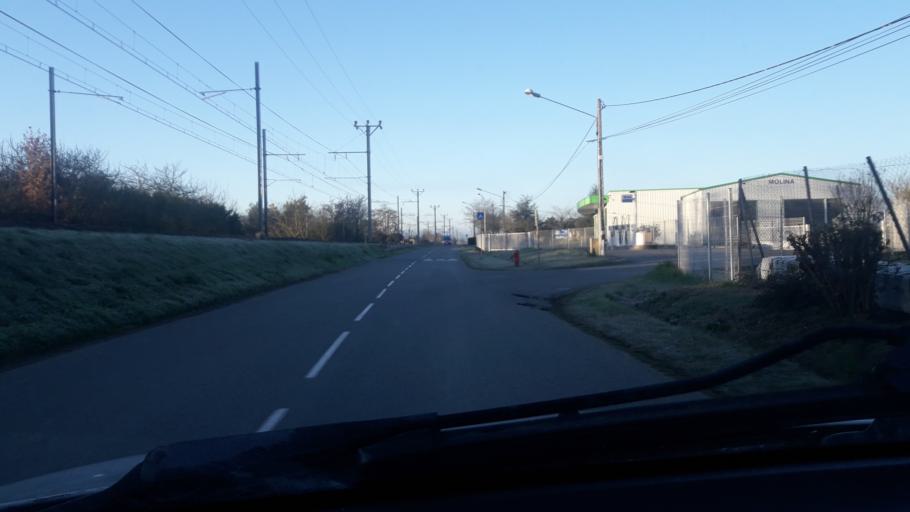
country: FR
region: Midi-Pyrenees
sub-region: Departement de la Haute-Garonne
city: Carbonne
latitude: 43.3056
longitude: 1.2211
